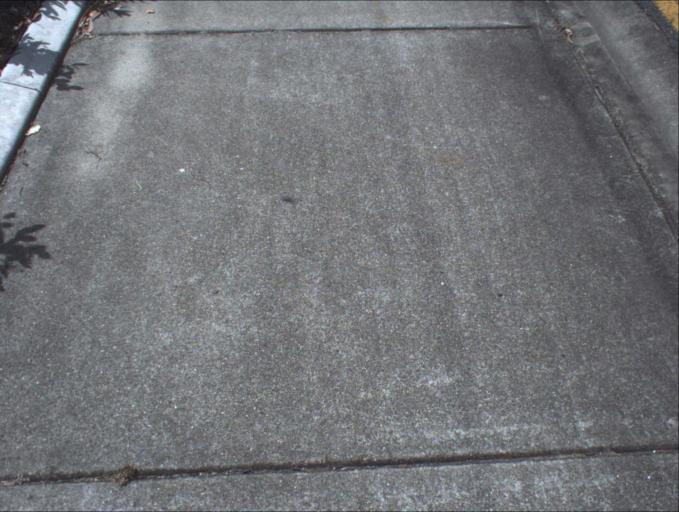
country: AU
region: Queensland
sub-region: Logan
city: Rochedale South
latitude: -27.6066
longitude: 153.1033
